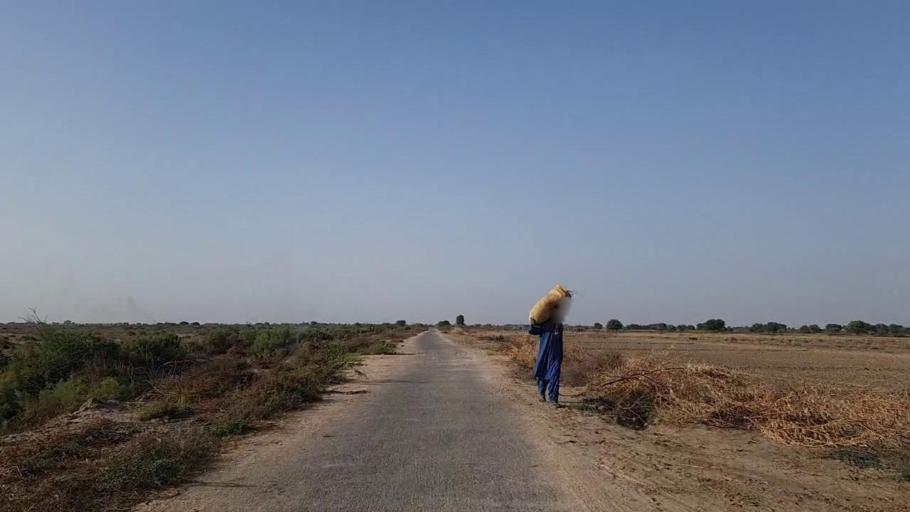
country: PK
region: Sindh
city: Jati
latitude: 24.3006
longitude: 68.1691
